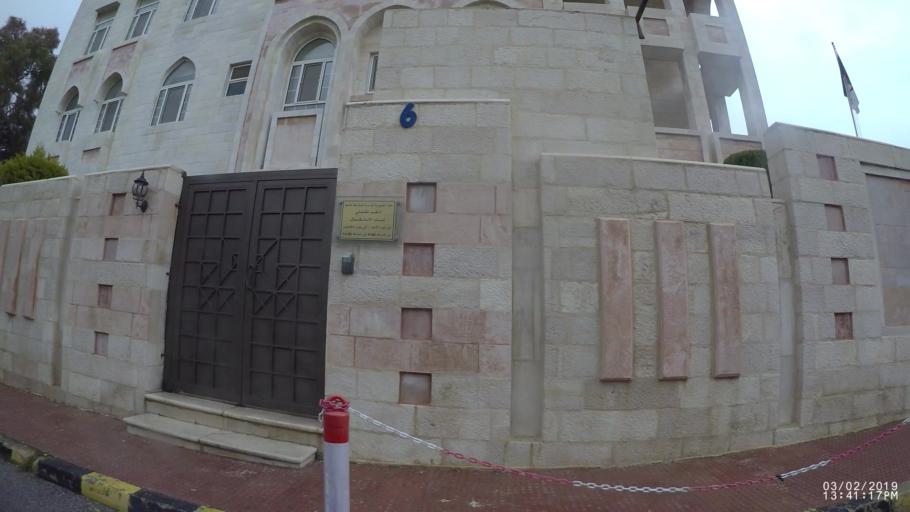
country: JO
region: Amman
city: Amman
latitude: 31.9574
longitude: 35.9041
